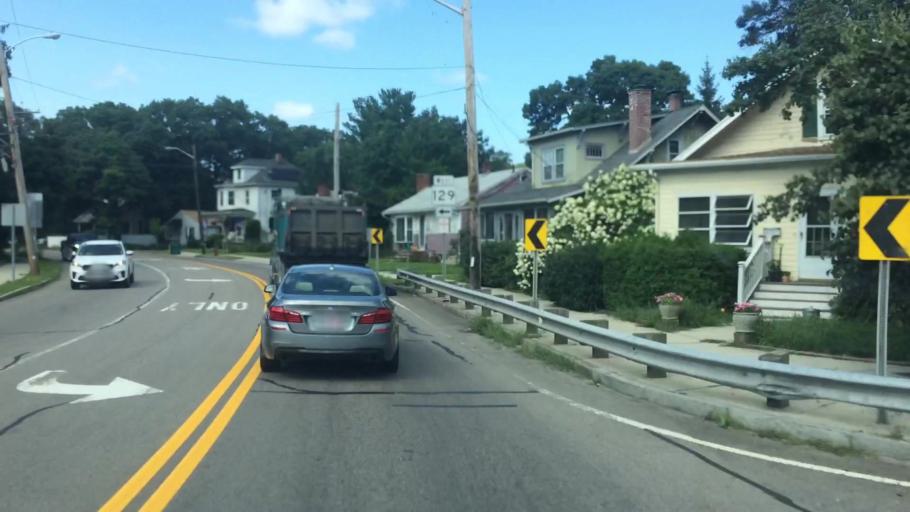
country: US
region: Massachusetts
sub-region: Essex County
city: South Peabody
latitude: 42.4965
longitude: -70.9699
